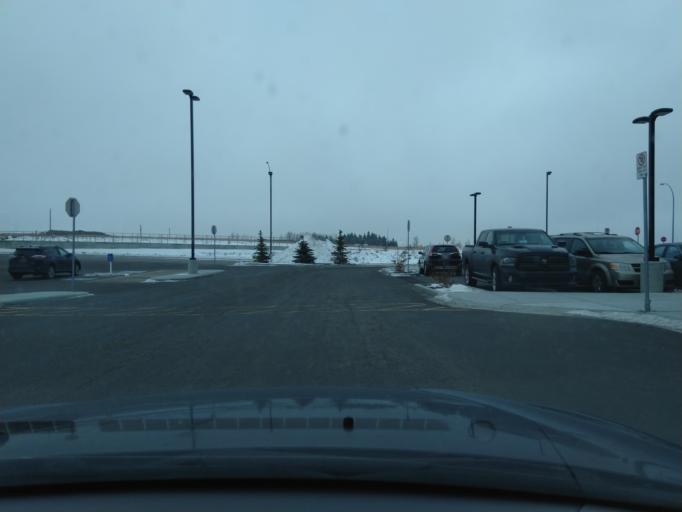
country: CA
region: Alberta
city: Airdrie
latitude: 51.1960
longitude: -113.9945
